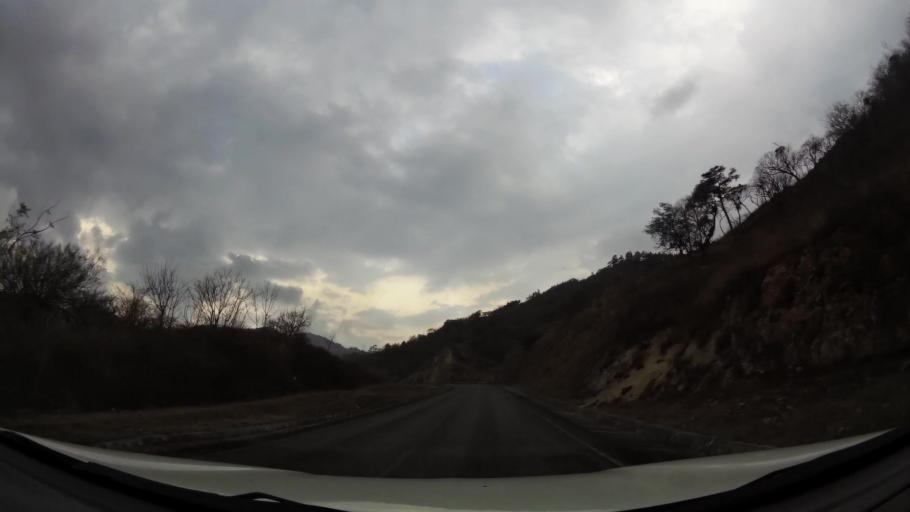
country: NI
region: Jinotega
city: Jinotega
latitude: 13.0555
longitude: -86.0033
